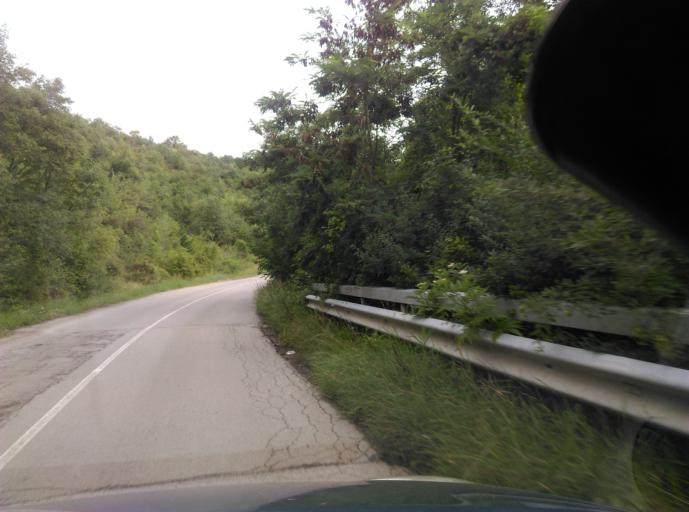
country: BG
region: Sofia-Capital
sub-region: Stolichna Obshtina
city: Sofia
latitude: 42.5879
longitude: 23.3996
